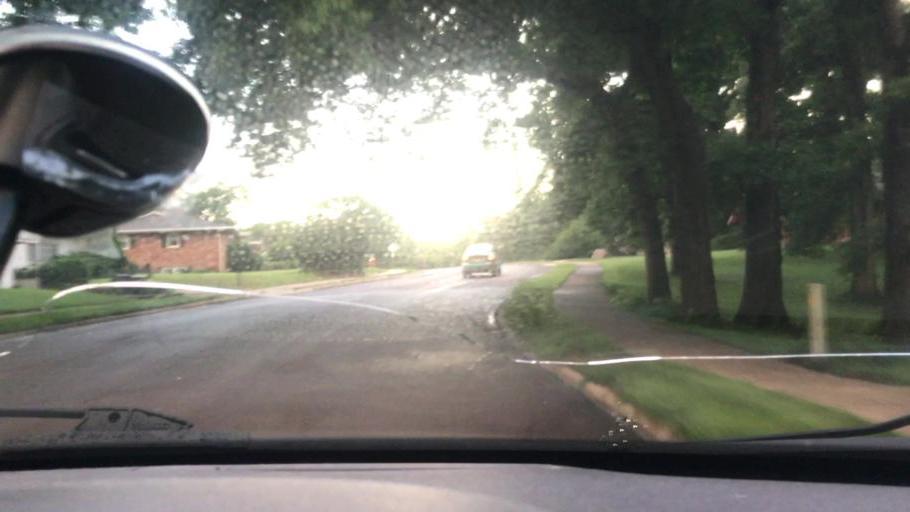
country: US
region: Illinois
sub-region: Tazewell County
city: Pekin
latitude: 40.5440
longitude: -89.6170
